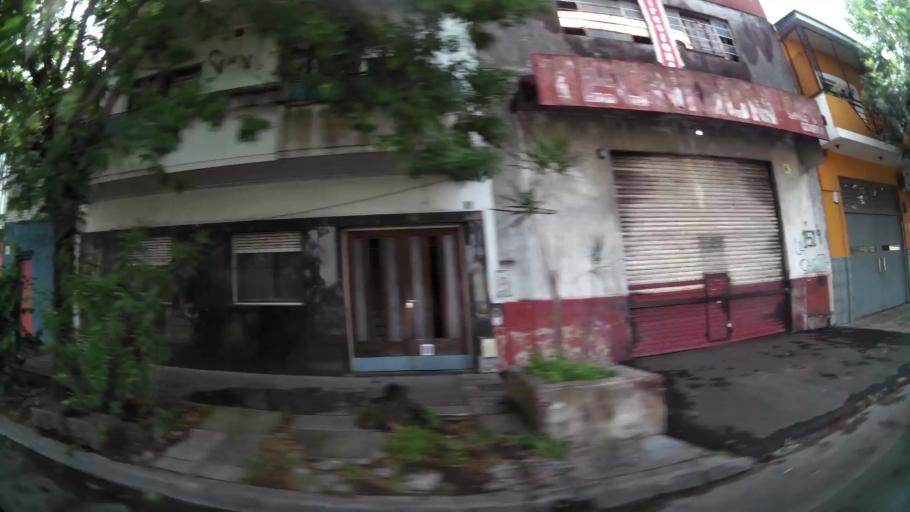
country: AR
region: Buenos Aires F.D.
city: Villa Lugano
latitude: -34.6498
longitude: -58.4263
